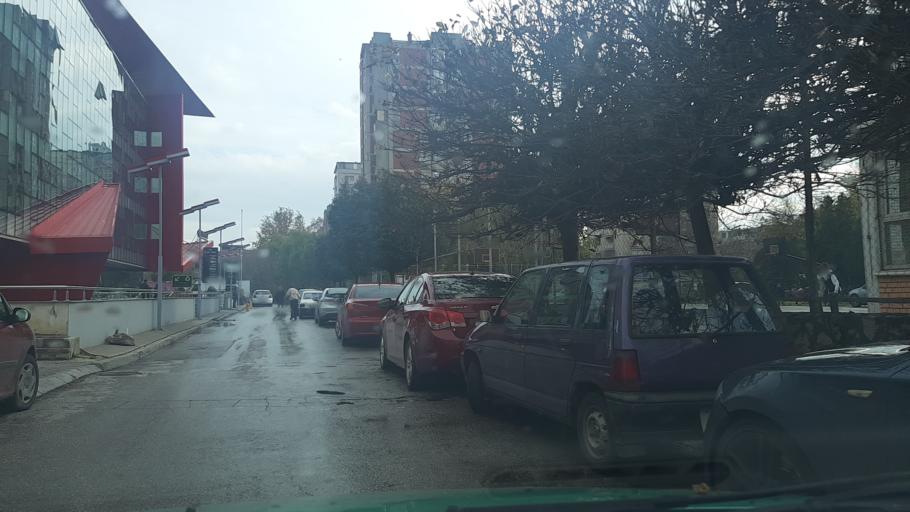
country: MK
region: Karpos
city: Skopje
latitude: 41.9917
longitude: 21.4515
